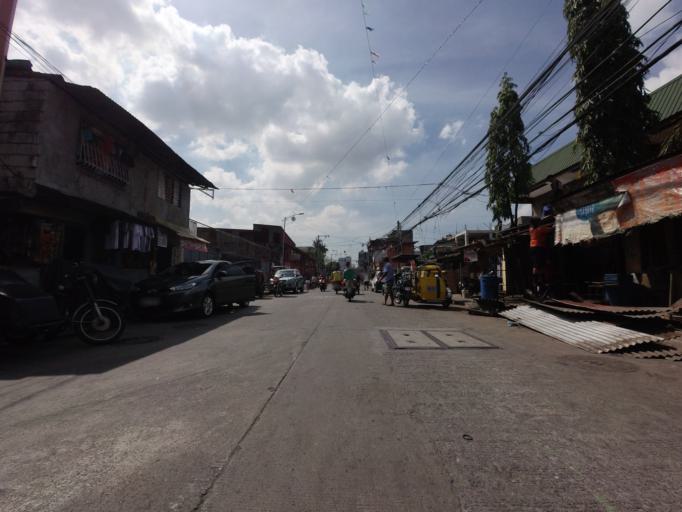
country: PH
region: Metro Manila
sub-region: Makati City
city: Makati City
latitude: 14.5736
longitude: 121.0083
